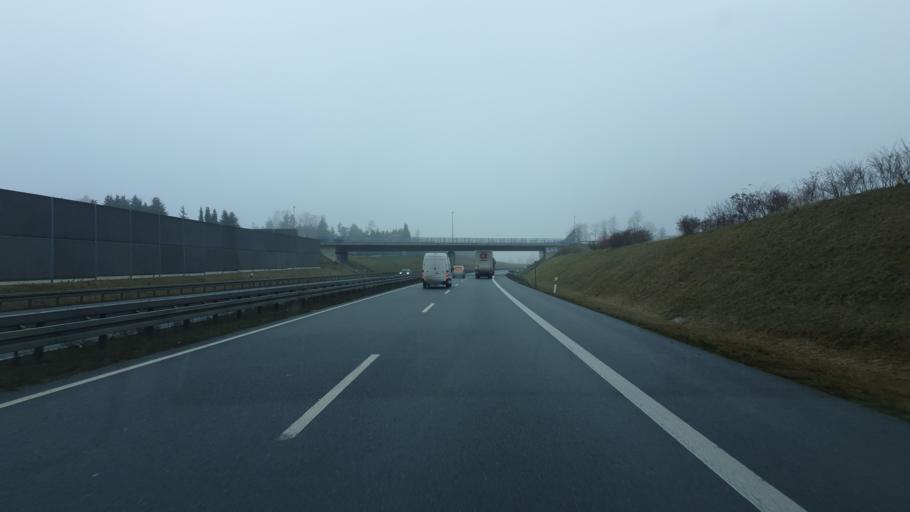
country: DE
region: Saxony
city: Hilbersdorf
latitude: 50.7959
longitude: 12.9828
